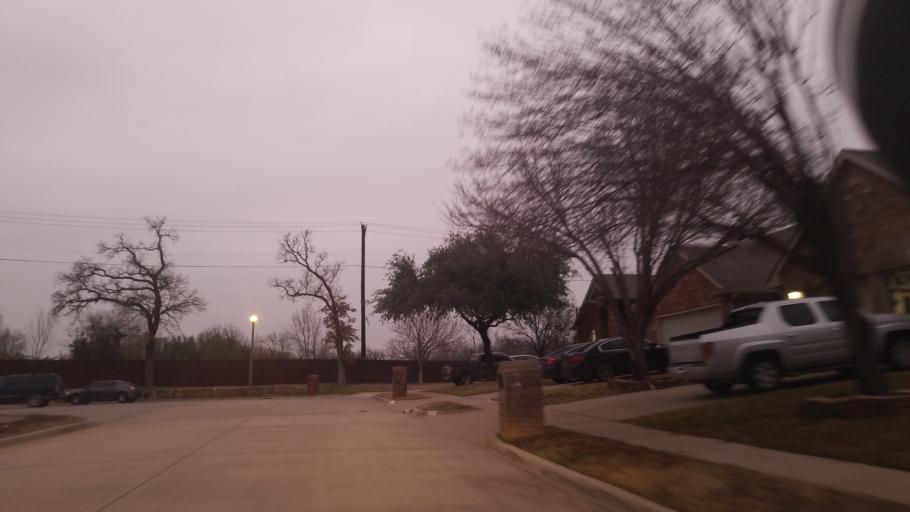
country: US
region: Texas
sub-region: Denton County
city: Corinth
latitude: 33.1622
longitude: -97.0915
